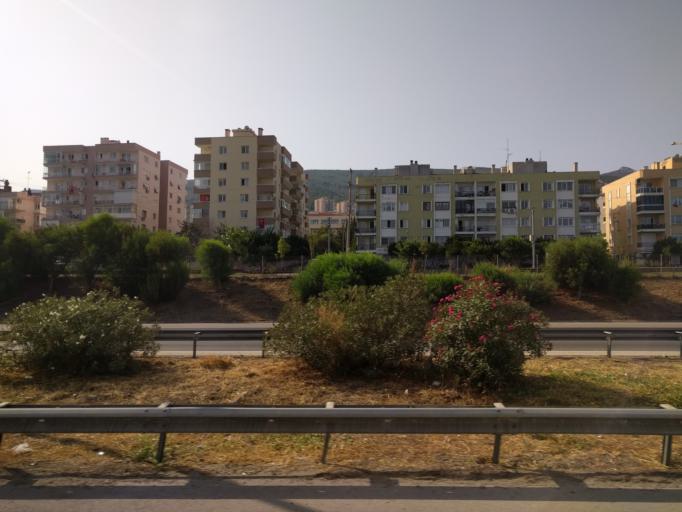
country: TR
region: Izmir
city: Karsiyaka
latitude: 38.3967
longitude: 26.9892
